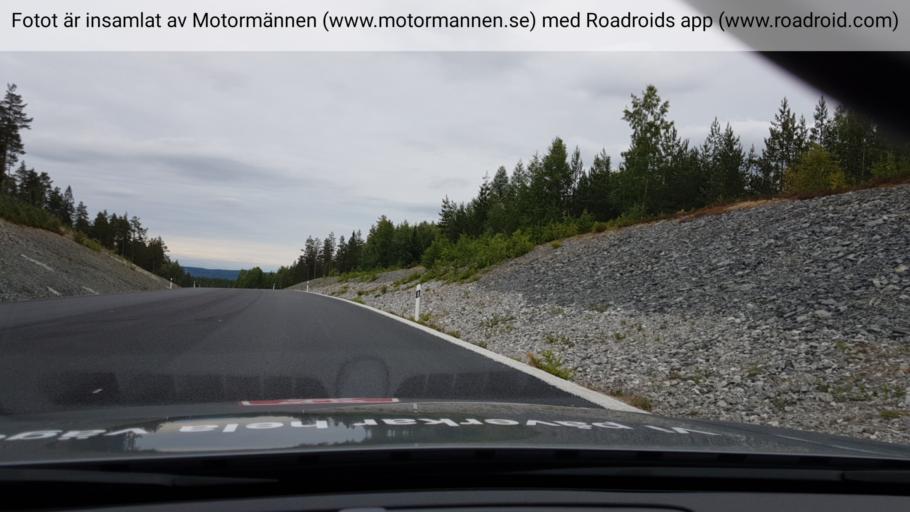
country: SE
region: Vaestmanland
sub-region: Skinnskattebergs Kommun
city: Skinnskatteberg
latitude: 59.8489
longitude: 15.5841
